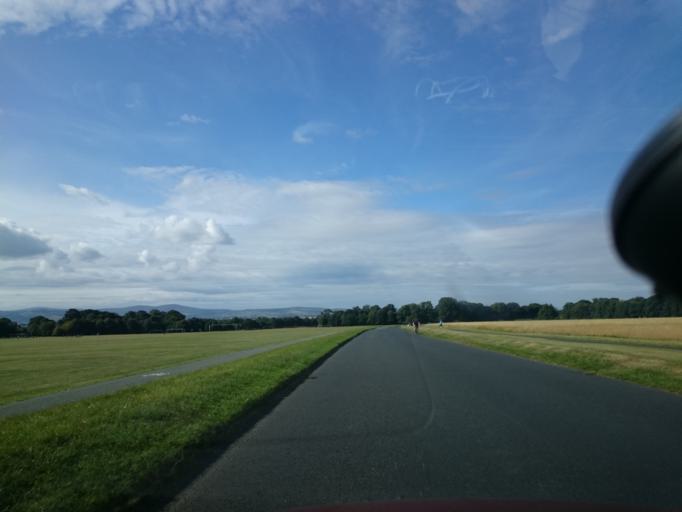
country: IE
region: Leinster
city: Chapelizod
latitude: 53.3525
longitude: -6.3280
